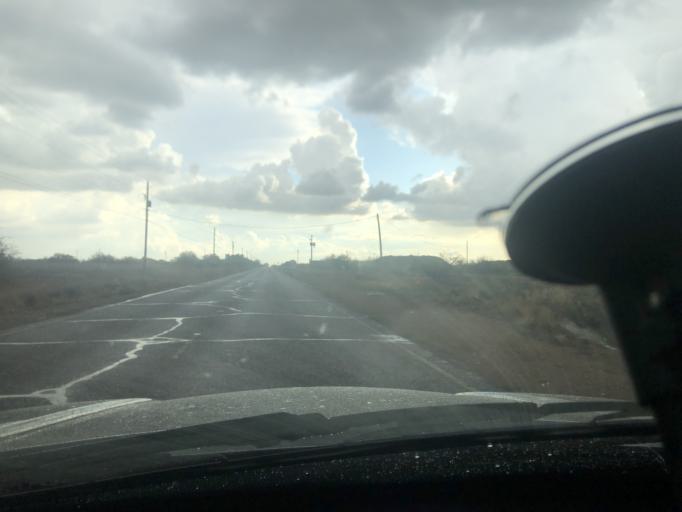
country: US
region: Arizona
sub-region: Maricopa County
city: Scottsdale
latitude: 33.4909
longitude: -111.8827
